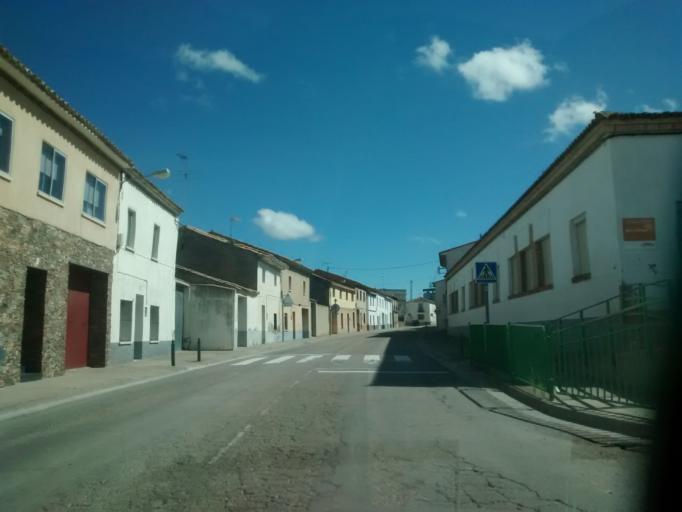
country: ES
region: Aragon
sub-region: Provincia de Zaragoza
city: Lecinena
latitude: 41.7981
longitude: -0.6099
